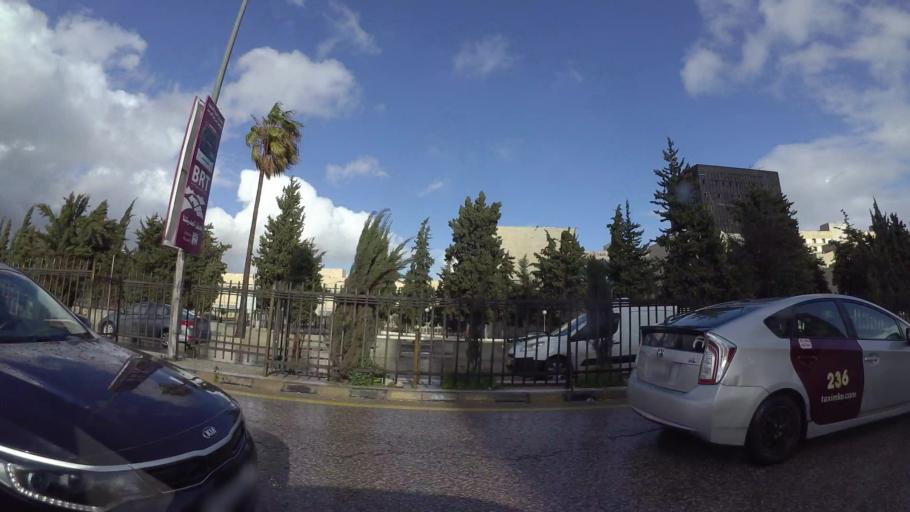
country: JO
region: Amman
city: Al Jubayhah
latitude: 32.0085
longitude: 35.8717
